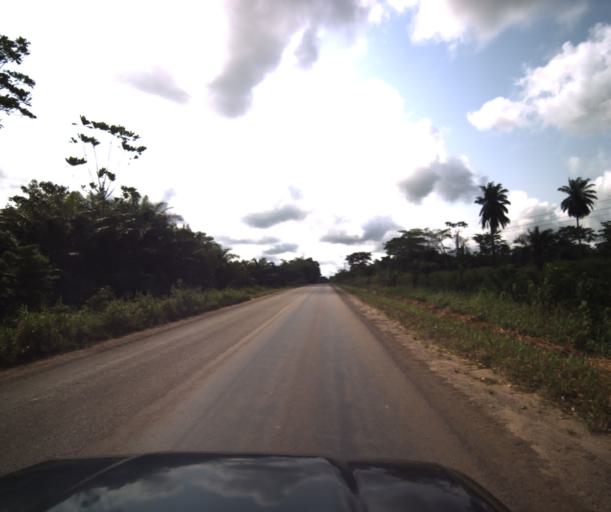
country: CM
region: Littoral
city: Edea
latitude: 3.7720
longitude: 10.1638
